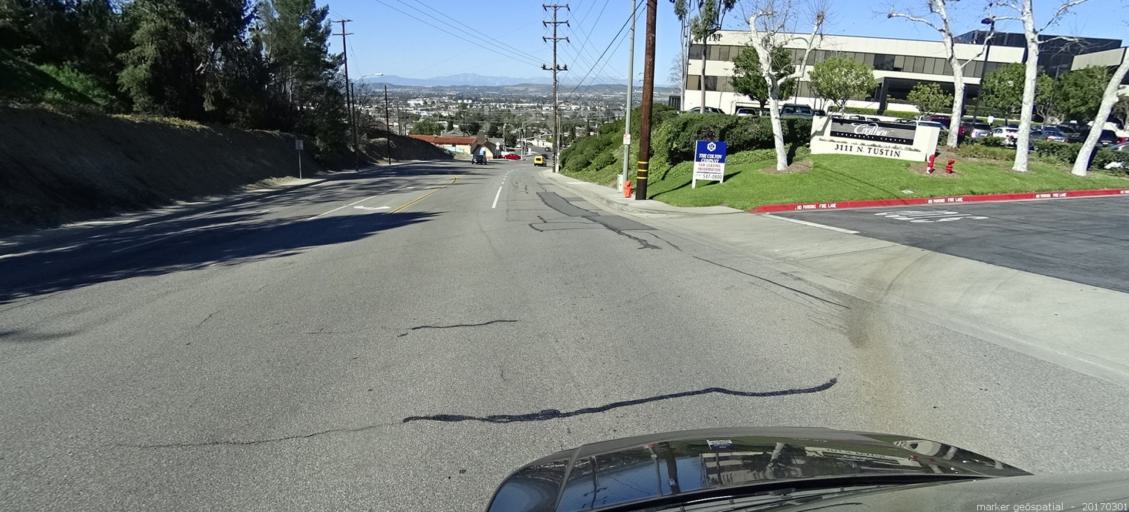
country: US
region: California
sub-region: Orange County
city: Villa Park
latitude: 33.8411
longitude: -117.8330
